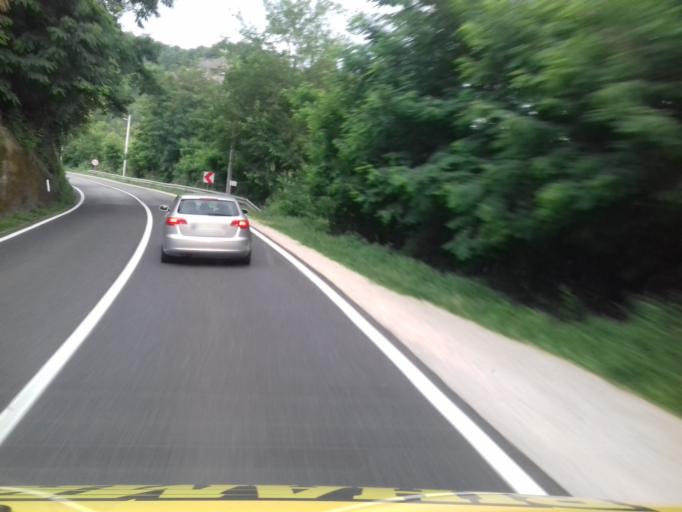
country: BA
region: Federation of Bosnia and Herzegovina
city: Konjic
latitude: 43.6870
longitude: 17.8752
